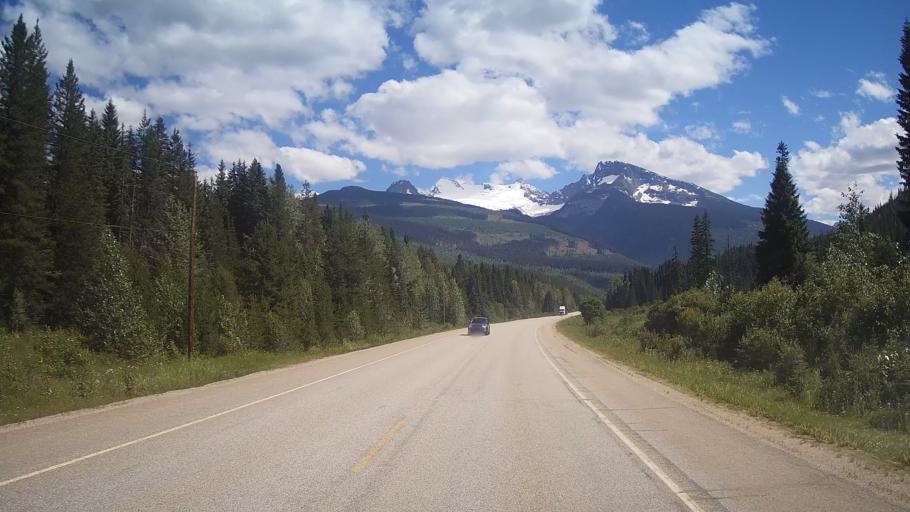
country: CA
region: Alberta
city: Jasper Park Lodge
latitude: 52.5951
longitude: -119.1023
